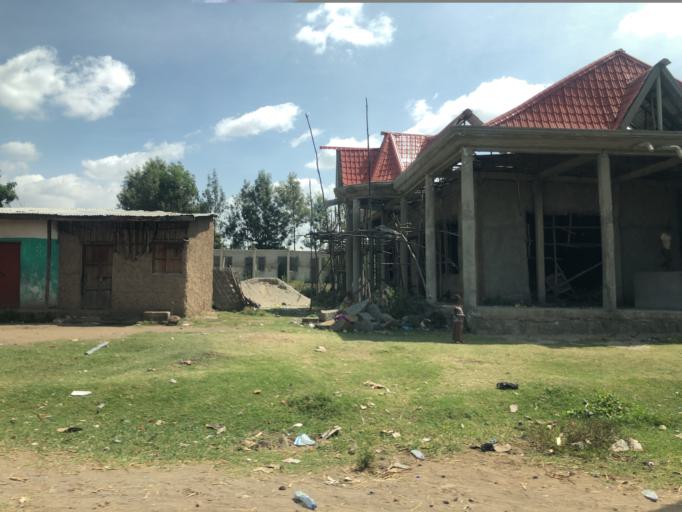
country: ET
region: Oromiya
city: Shashemene
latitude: 7.2226
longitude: 38.6266
